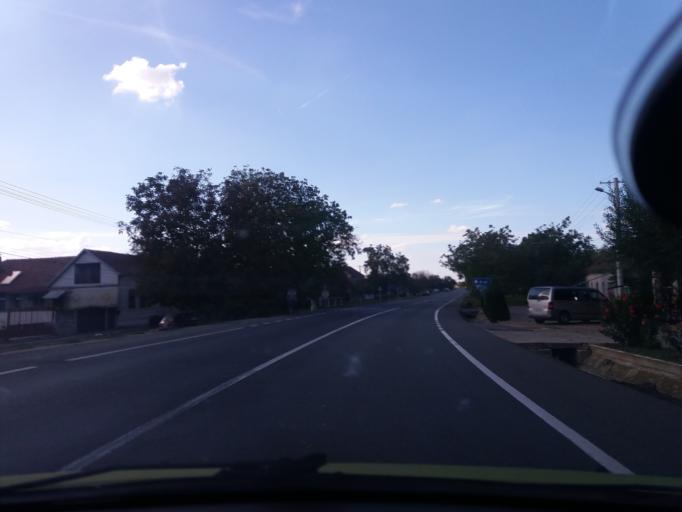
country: RO
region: Arad
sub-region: Comuna Paulis
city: Paulis
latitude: 46.1119
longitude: 21.5965
